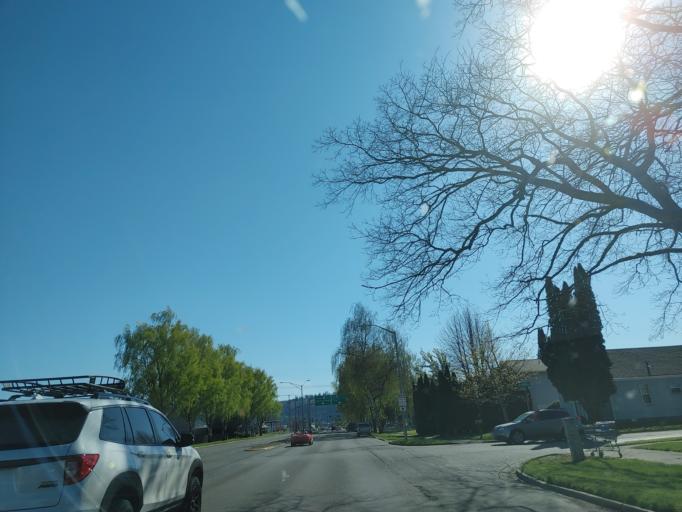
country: US
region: Washington
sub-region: Cowlitz County
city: Longview
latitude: 46.1193
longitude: -122.9482
